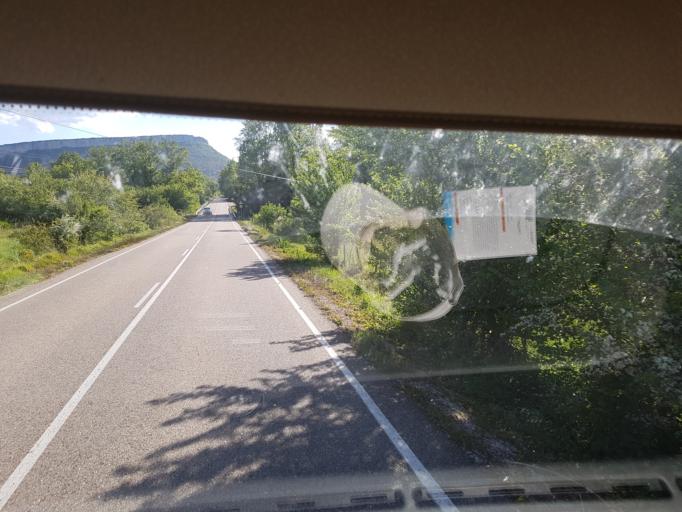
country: ES
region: Castille and Leon
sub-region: Provincia de Burgos
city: Espinosa de los Monteros
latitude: 43.0560
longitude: -3.6113
